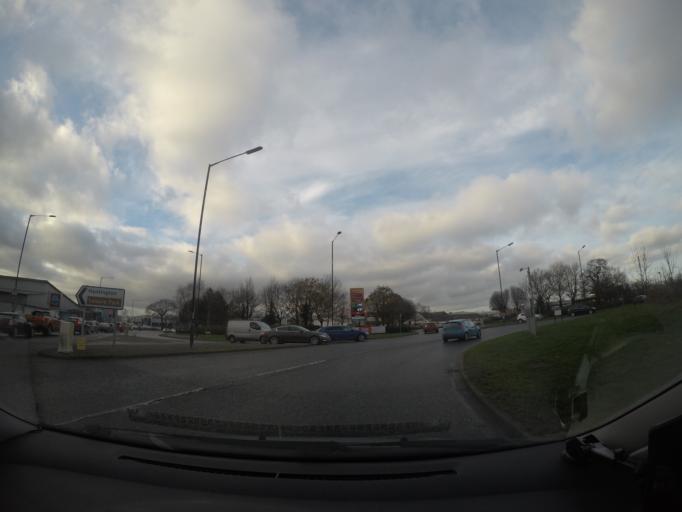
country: GB
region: England
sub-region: City of York
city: Huntington
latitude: 53.9855
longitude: -1.0473
